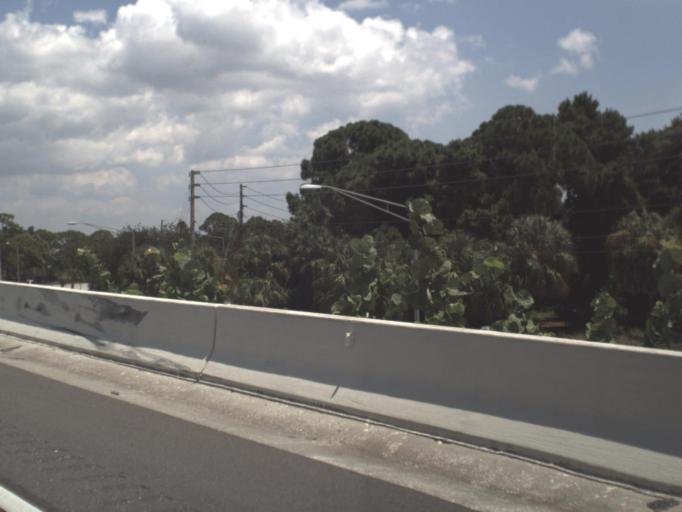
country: US
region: Florida
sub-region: Pinellas County
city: Tierra Verde
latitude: 27.7077
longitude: -82.6791
